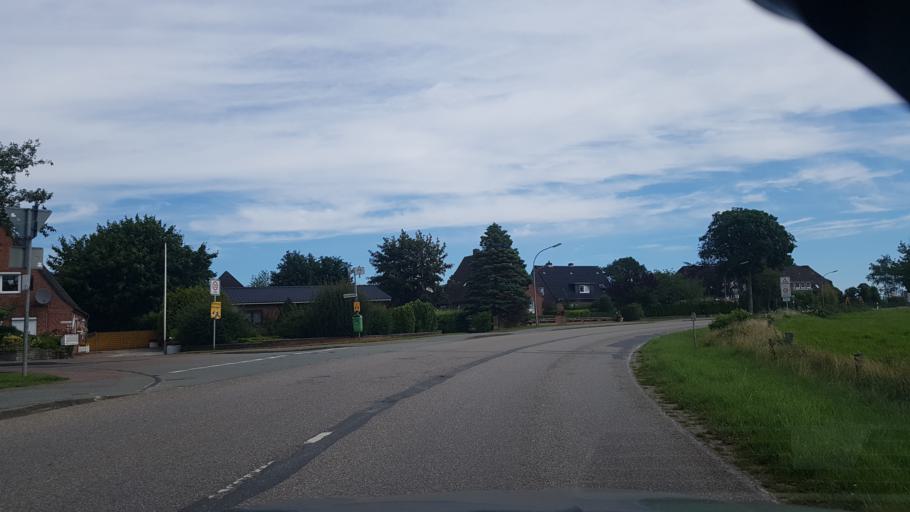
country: DE
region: Schleswig-Holstein
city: Ladelund
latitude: 54.8409
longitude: 9.0284
